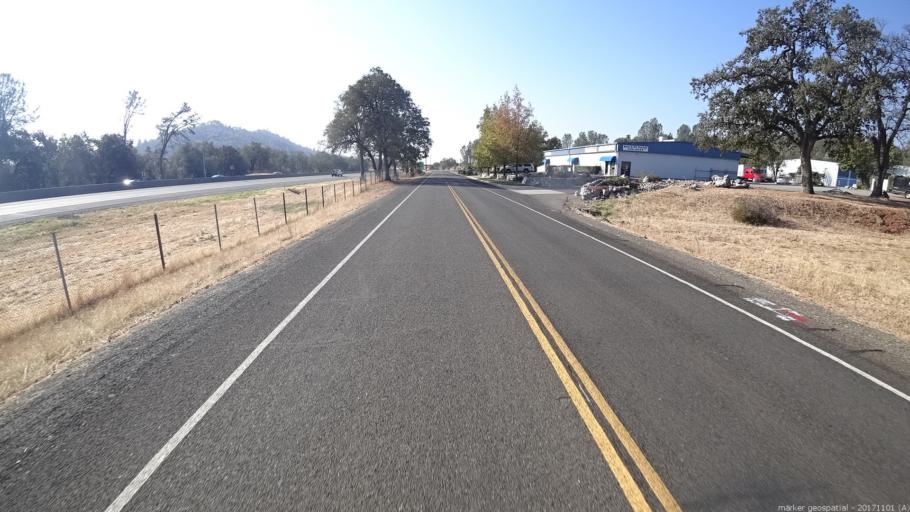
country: US
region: California
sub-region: Shasta County
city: Shasta Lake
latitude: 40.7109
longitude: -122.3345
